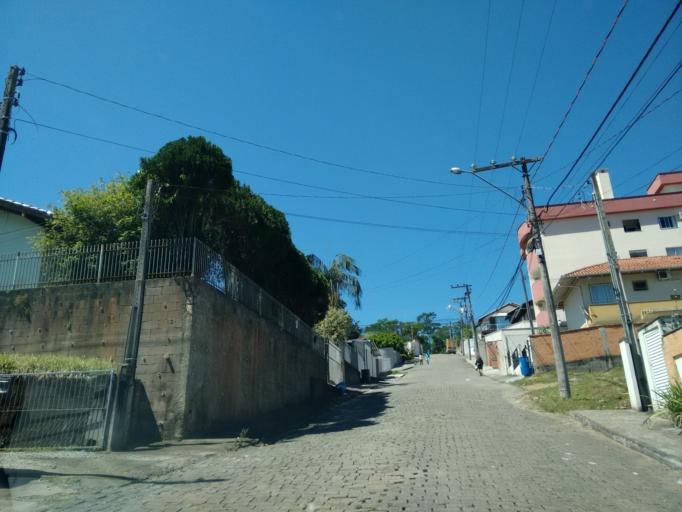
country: BR
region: Santa Catarina
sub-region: Blumenau
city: Blumenau
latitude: -26.8922
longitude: -49.1054
